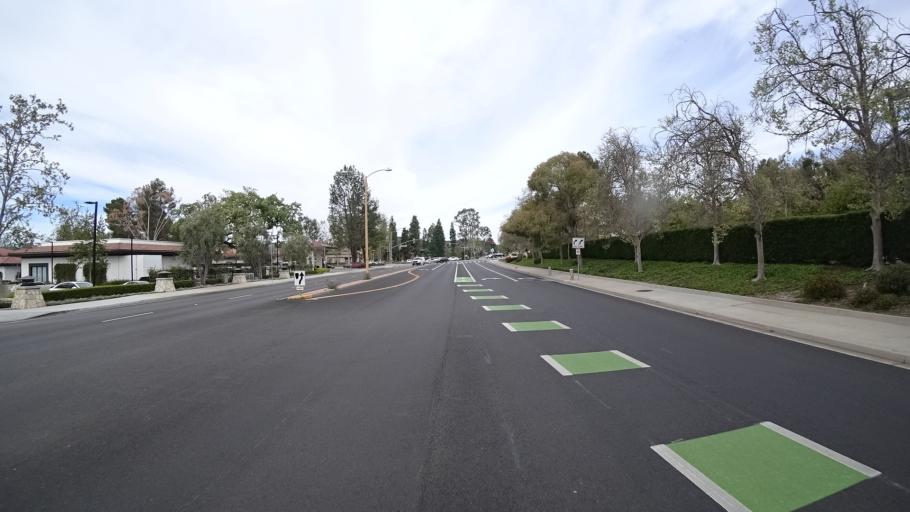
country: US
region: California
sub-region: Ventura County
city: Thousand Oaks
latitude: 34.1542
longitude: -118.8260
